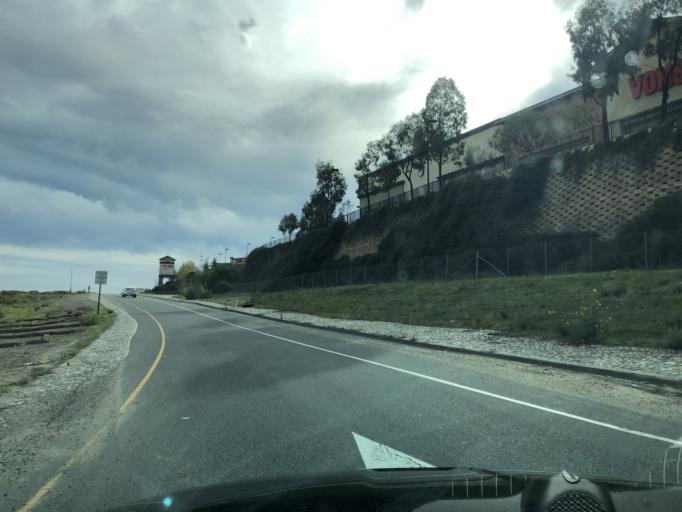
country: US
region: California
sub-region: Riverside County
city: El Cerrito
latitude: 33.7481
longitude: -117.4533
